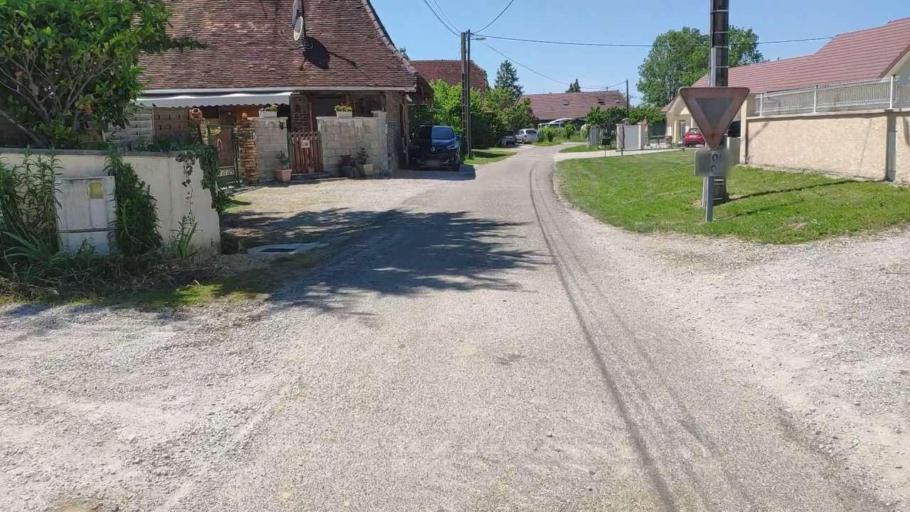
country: FR
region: Franche-Comte
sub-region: Departement du Jura
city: Bletterans
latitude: 46.7423
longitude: 5.3682
